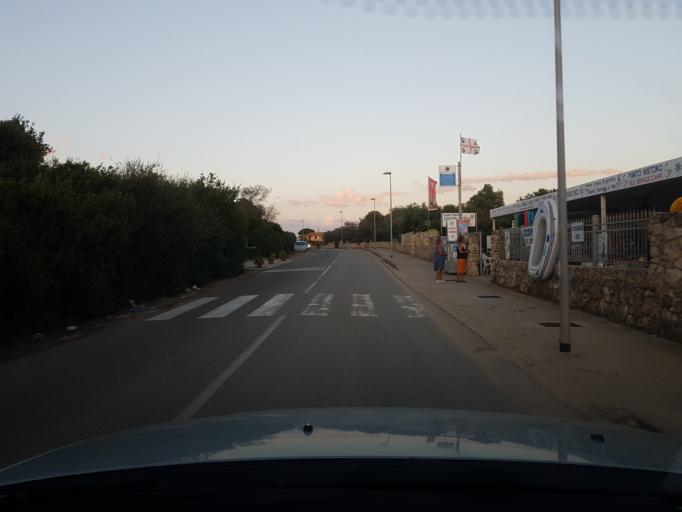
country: IT
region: Sardinia
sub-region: Provincia di Oristano
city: Riola Sardo
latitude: 40.0281
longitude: 8.4095
